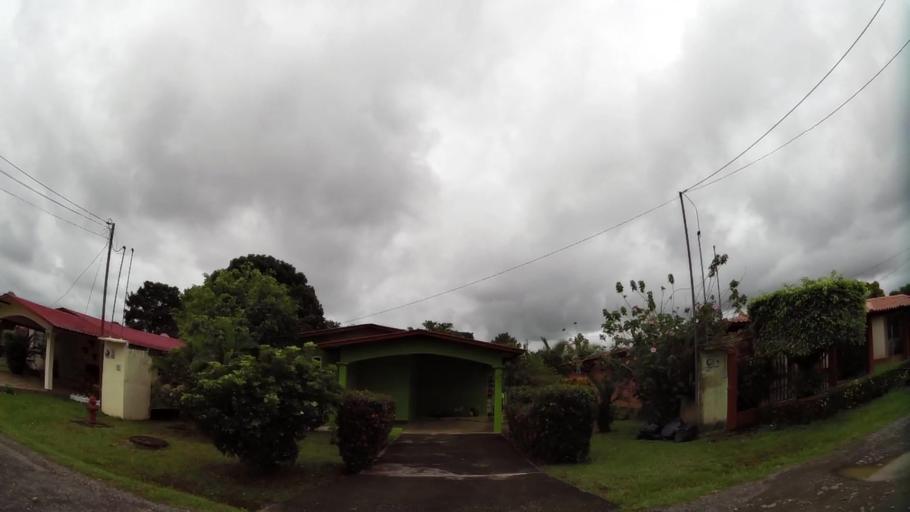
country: PA
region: Chiriqui
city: David
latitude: 8.4160
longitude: -82.4549
